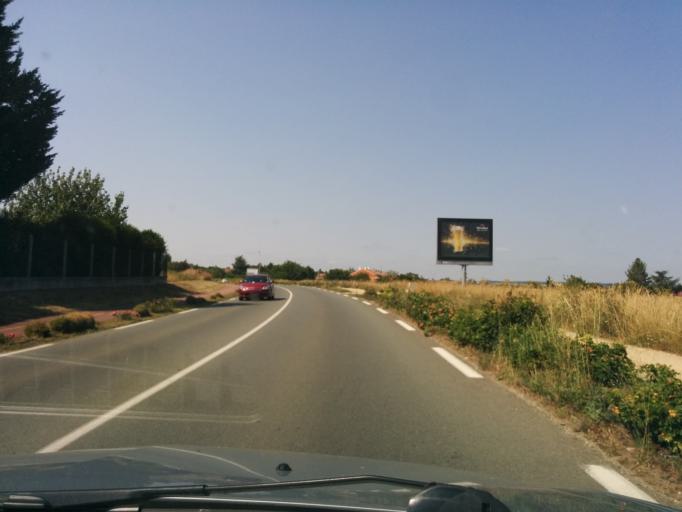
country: FR
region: Poitou-Charentes
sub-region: Departement de la Vienne
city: Jaunay-Clan
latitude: 46.6775
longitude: 0.3658
